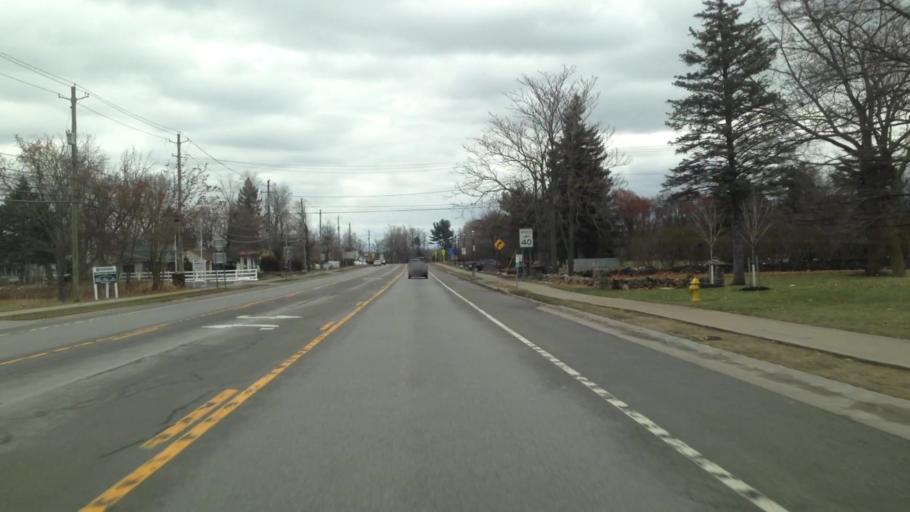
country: US
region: New York
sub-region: Erie County
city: Clarence
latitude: 42.9792
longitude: -78.6029
